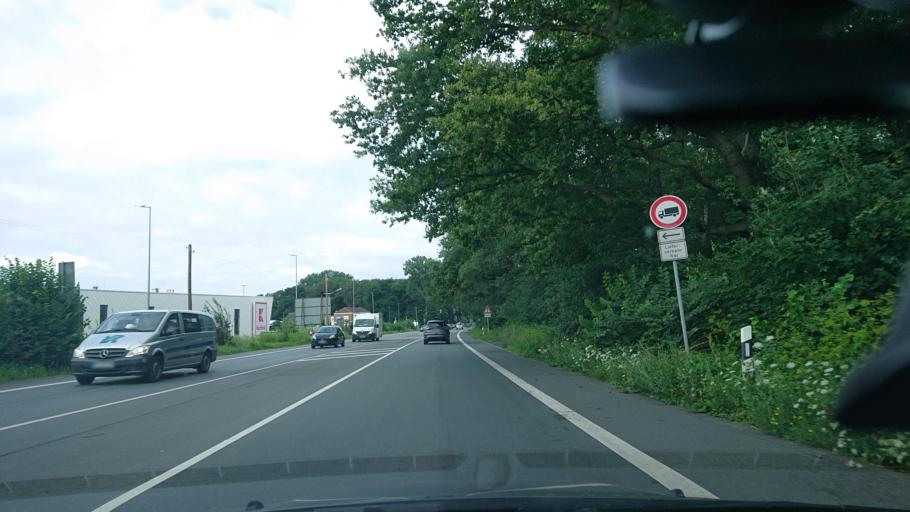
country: DE
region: North Rhine-Westphalia
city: Werne
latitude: 51.6523
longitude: 7.6792
